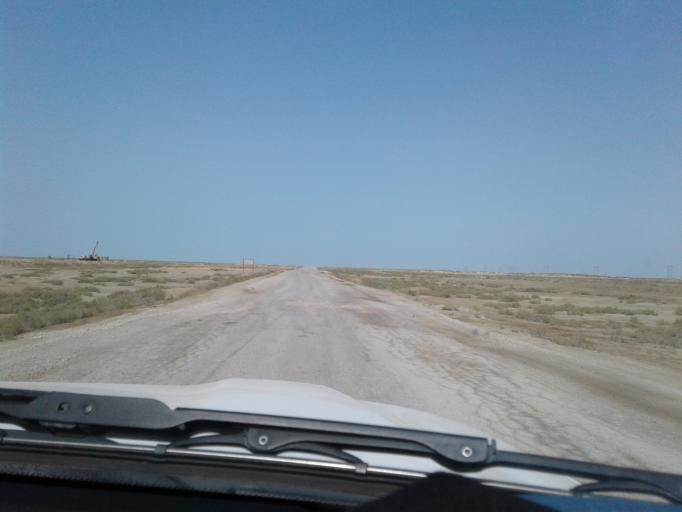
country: IR
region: Golestan
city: Gomishan
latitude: 37.8355
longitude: 53.9071
